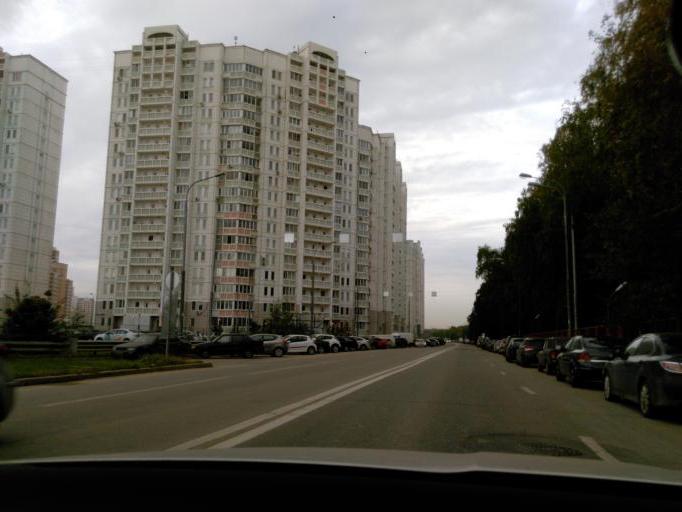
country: RU
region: Moscow
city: Severnyy
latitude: 55.9297
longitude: 37.5455
